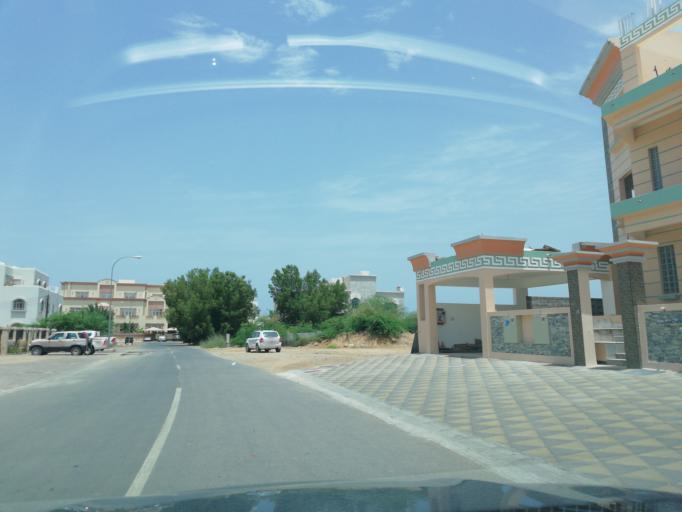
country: OM
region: Muhafazat Masqat
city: As Sib al Jadidah
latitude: 23.6215
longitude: 58.2594
